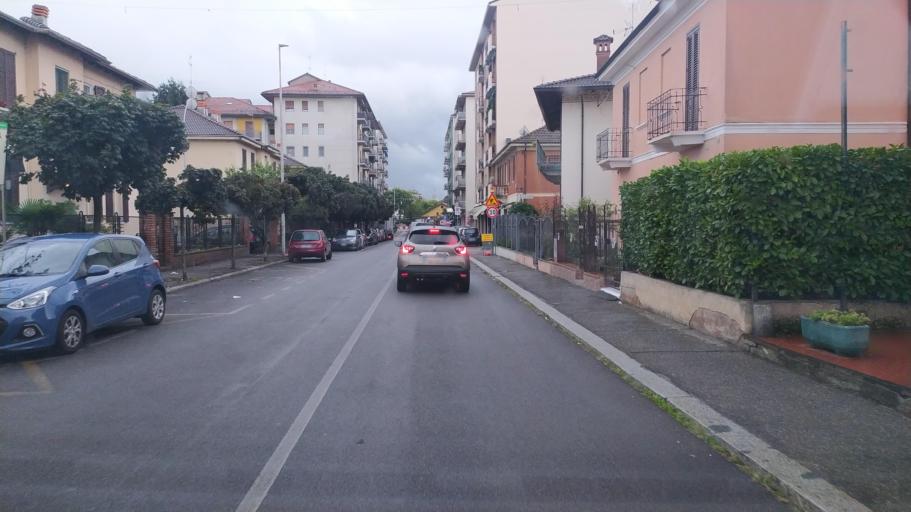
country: IT
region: Lombardy
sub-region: Provincia di Pavia
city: Pavia
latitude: 45.1995
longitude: 9.1593
